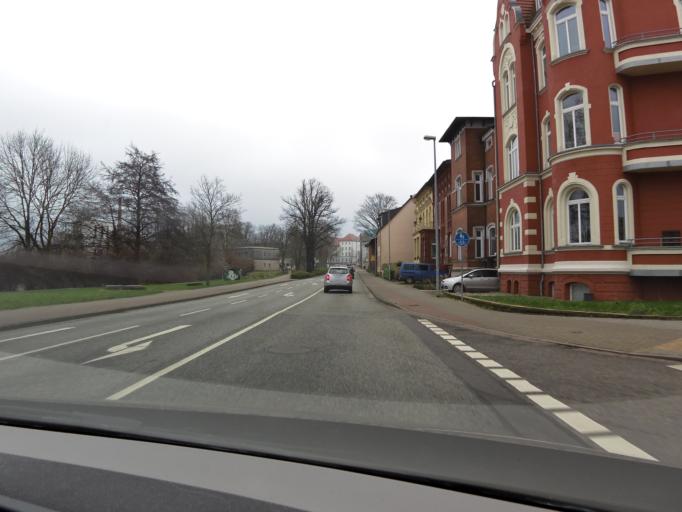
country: DE
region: Mecklenburg-Vorpommern
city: Schelfstadt
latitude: 53.6367
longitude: 11.4189
